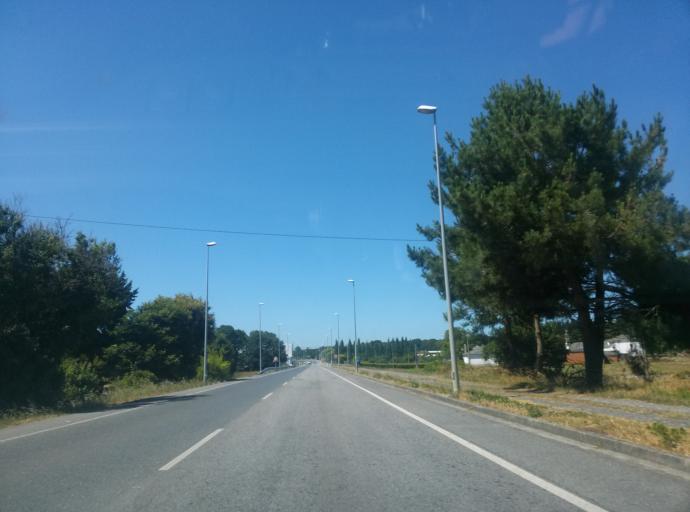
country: ES
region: Galicia
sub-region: Provincia de Lugo
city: Mos
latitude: 43.1309
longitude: -7.4887
